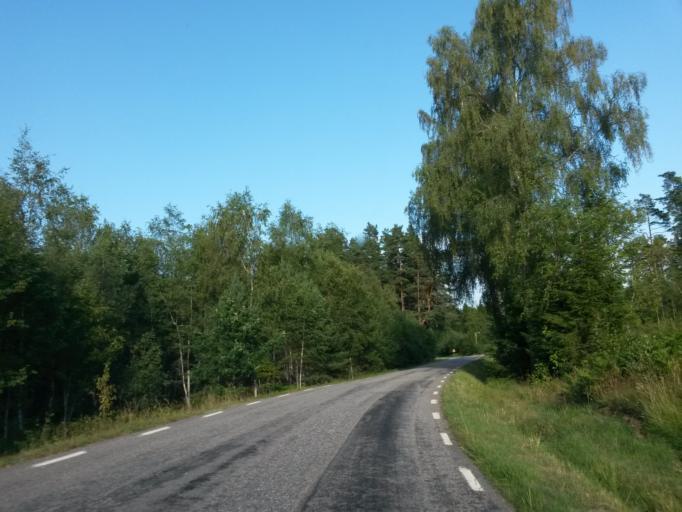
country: SE
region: Vaestra Goetaland
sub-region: Vara Kommun
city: Vara
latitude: 58.2783
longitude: 12.8450
